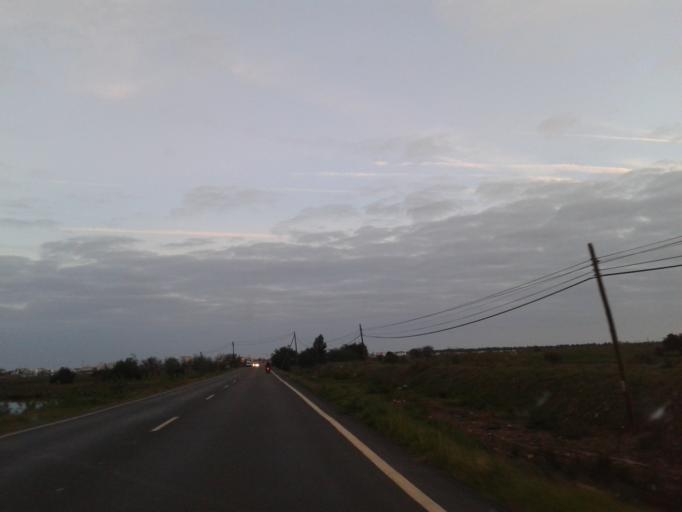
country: PT
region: Faro
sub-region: Castro Marim
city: Castro Marim
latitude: 37.2085
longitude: -7.4362
